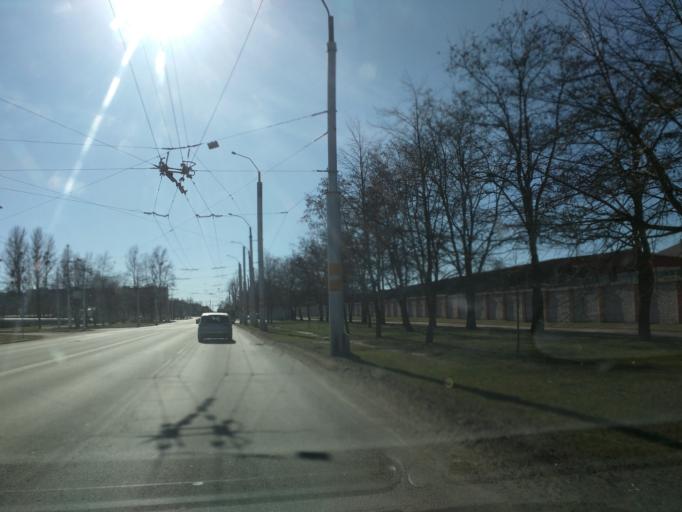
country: BY
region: Mogilev
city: Babruysk
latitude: 53.1797
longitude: 29.2027
